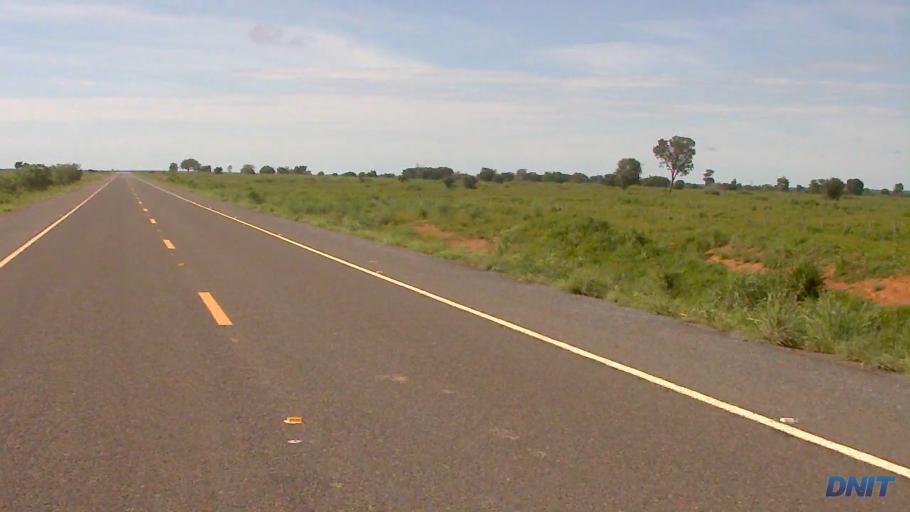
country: BR
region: Goias
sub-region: Sao Miguel Do Araguaia
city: Sao Miguel do Araguaia
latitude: -13.4732
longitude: -50.1141
